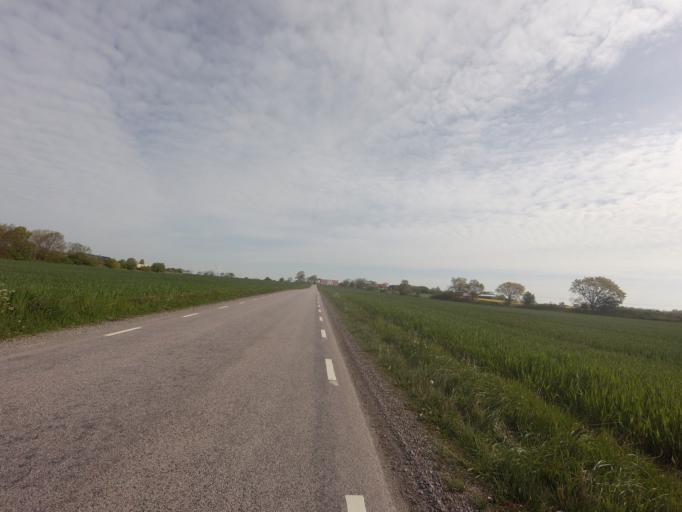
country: SE
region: Skane
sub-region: Hoganas Kommun
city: Hoganas
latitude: 56.2076
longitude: 12.5785
